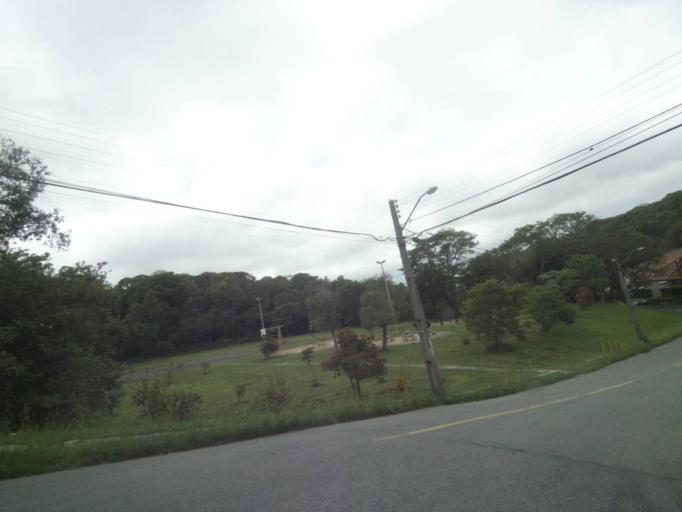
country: BR
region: Parana
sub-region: Curitiba
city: Curitiba
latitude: -25.3908
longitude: -49.2794
